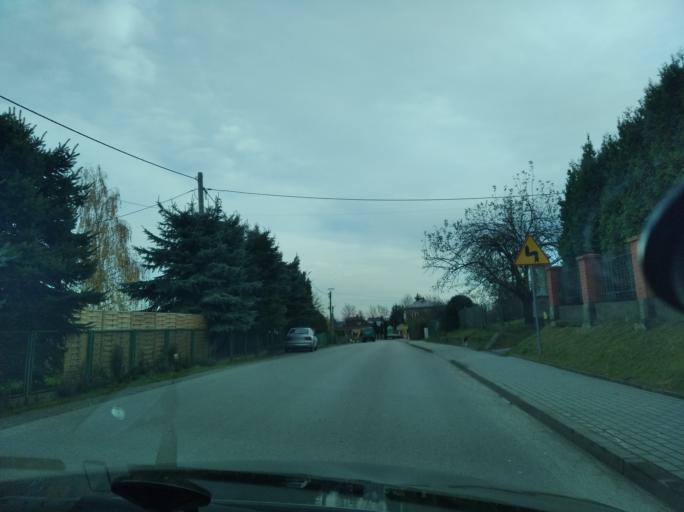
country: PL
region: Subcarpathian Voivodeship
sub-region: Powiat przeworski
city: Debow
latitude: 50.0445
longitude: 22.4394
